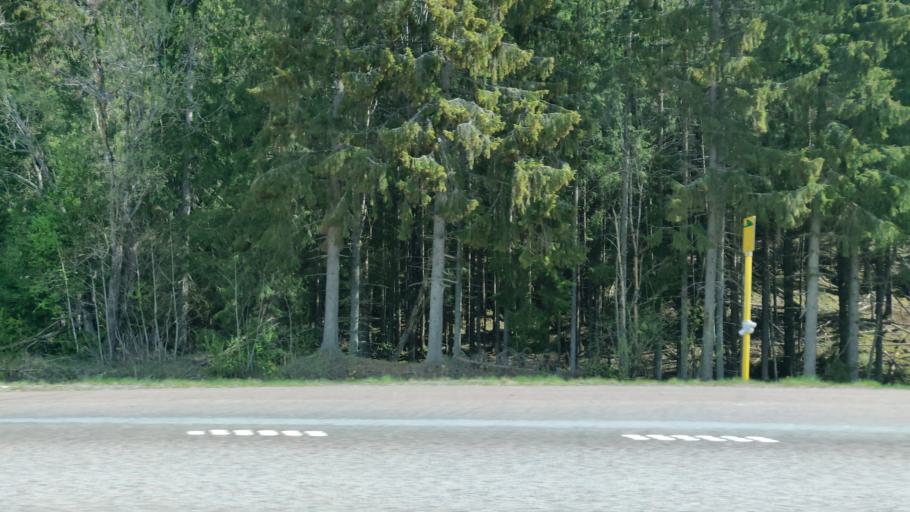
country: SE
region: Vaermland
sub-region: Karlstads Kommun
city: Molkom
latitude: 59.5675
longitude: 13.6662
